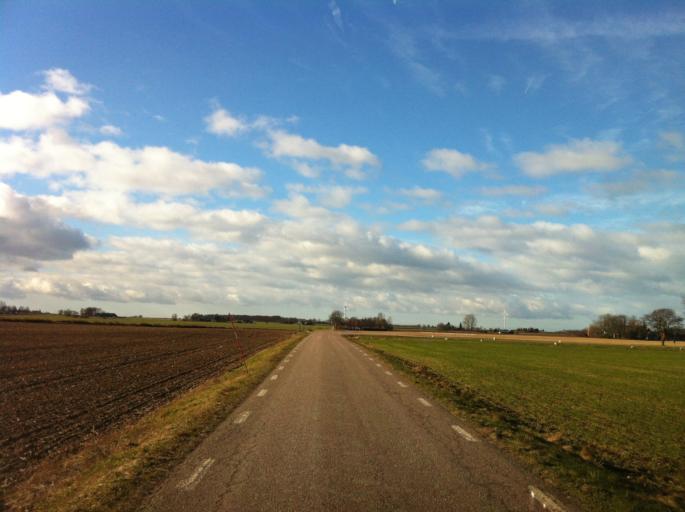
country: SE
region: Skane
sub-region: Svalovs Kommun
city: Svaloev
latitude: 55.9378
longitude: 13.0197
